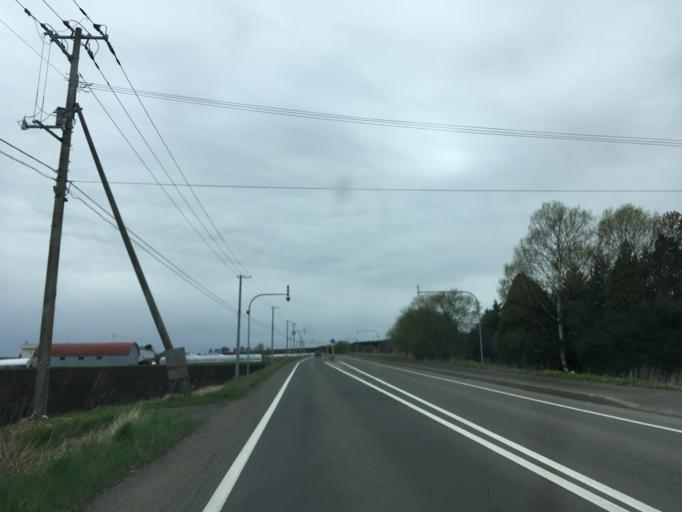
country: JP
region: Hokkaido
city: Chitose
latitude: 42.9471
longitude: 141.7731
